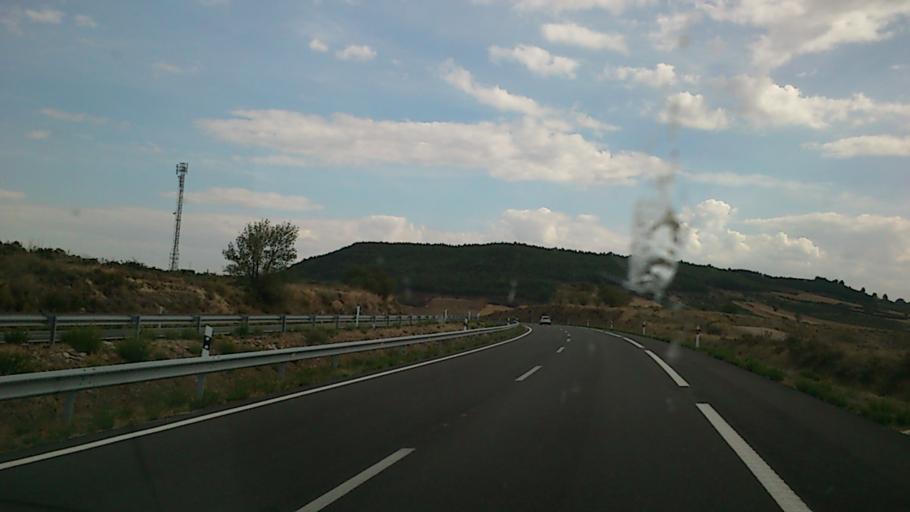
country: ES
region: La Rioja
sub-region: Provincia de La Rioja
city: Briones
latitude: 42.5266
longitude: -2.7848
